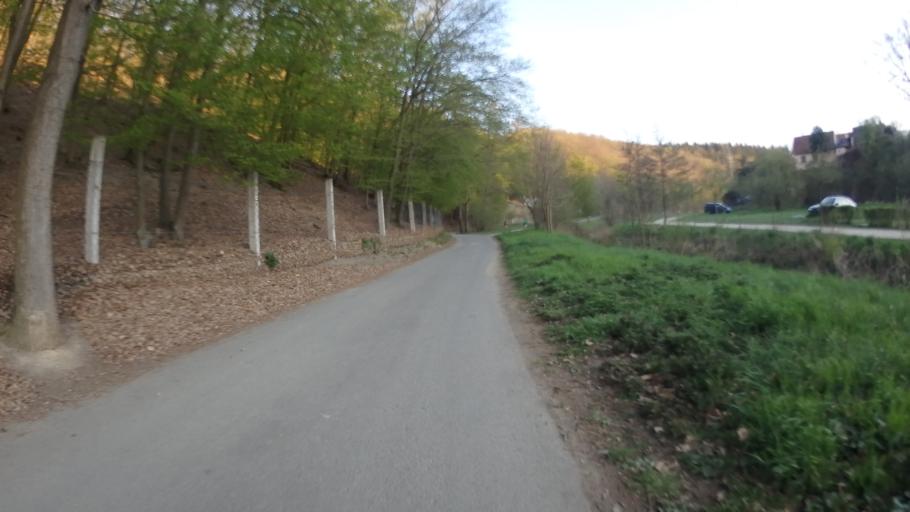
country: CZ
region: South Moravian
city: Troubsko
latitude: 49.2146
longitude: 16.5268
